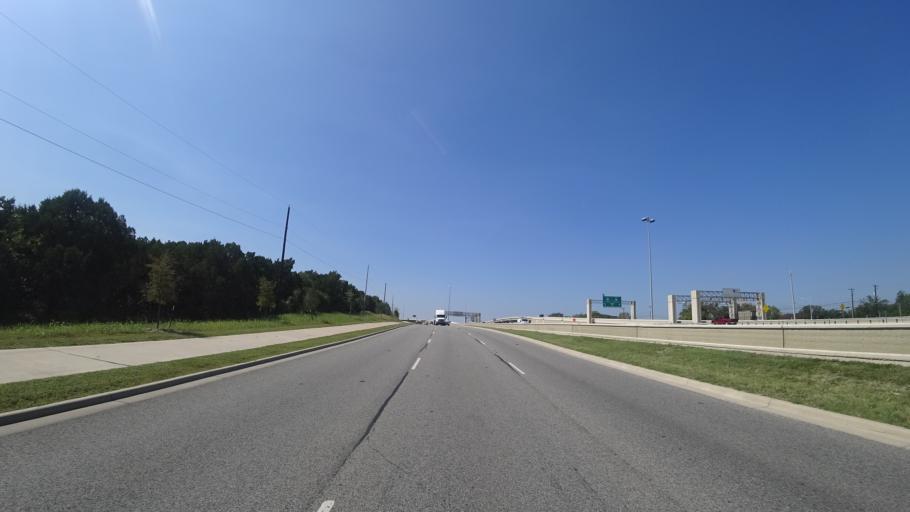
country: US
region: Texas
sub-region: Travis County
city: Austin
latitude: 30.3274
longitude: -97.6649
